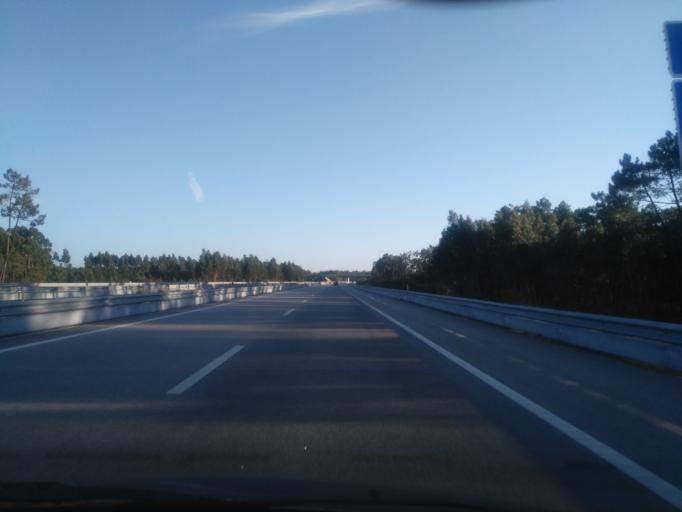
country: PT
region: Coimbra
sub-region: Figueira da Foz
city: Alhadas
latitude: 40.2405
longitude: -8.7841
